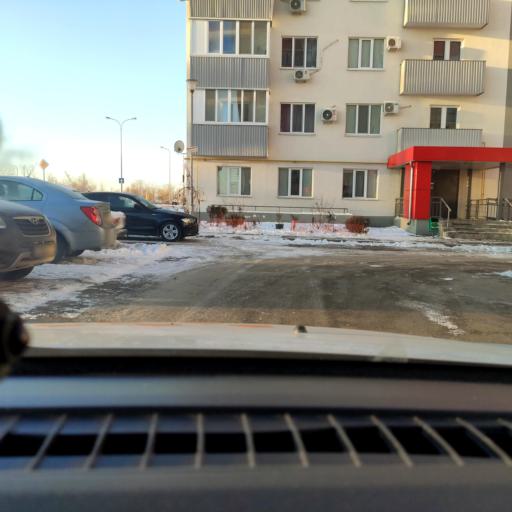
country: RU
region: Samara
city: Samara
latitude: 53.0939
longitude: 50.1665
